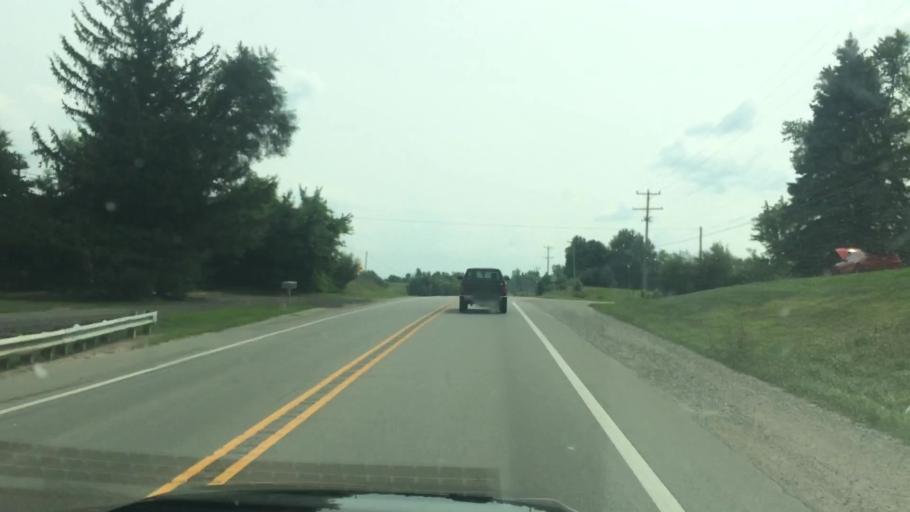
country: US
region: Michigan
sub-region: Oakland County
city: Oxford
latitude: 42.9273
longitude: -83.3130
